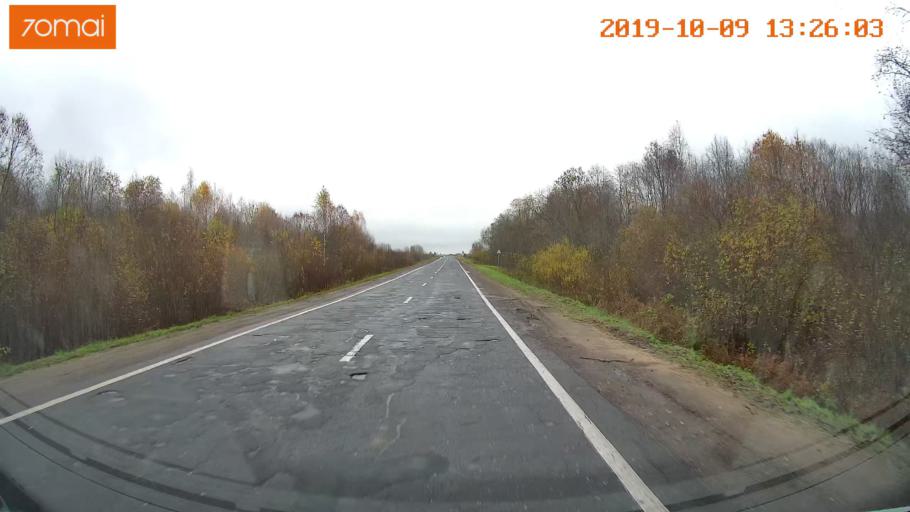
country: RU
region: Jaroslavl
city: Lyubim
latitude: 58.3235
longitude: 40.9200
